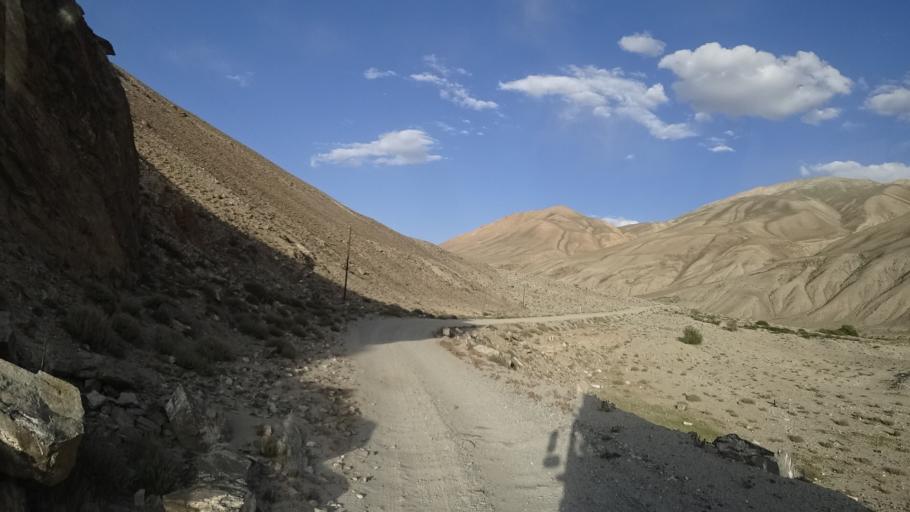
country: AF
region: Badakhshan
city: Khandud
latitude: 37.2311
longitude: 72.8537
